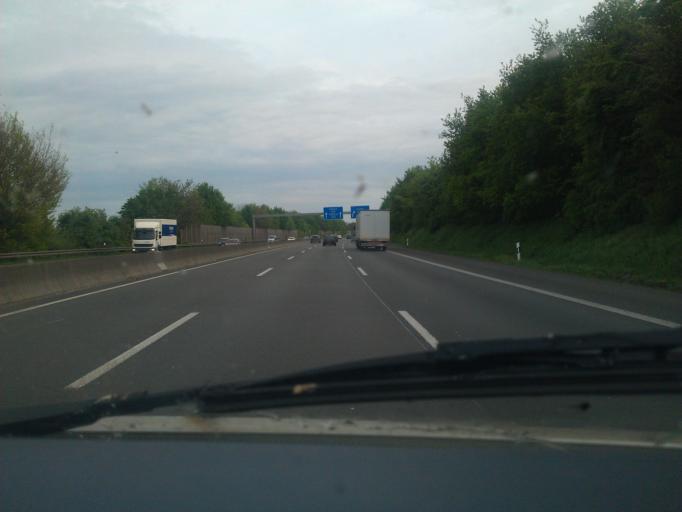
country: DE
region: North Rhine-Westphalia
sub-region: Regierungsbezirk Koln
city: Titz
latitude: 51.0577
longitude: 6.4443
